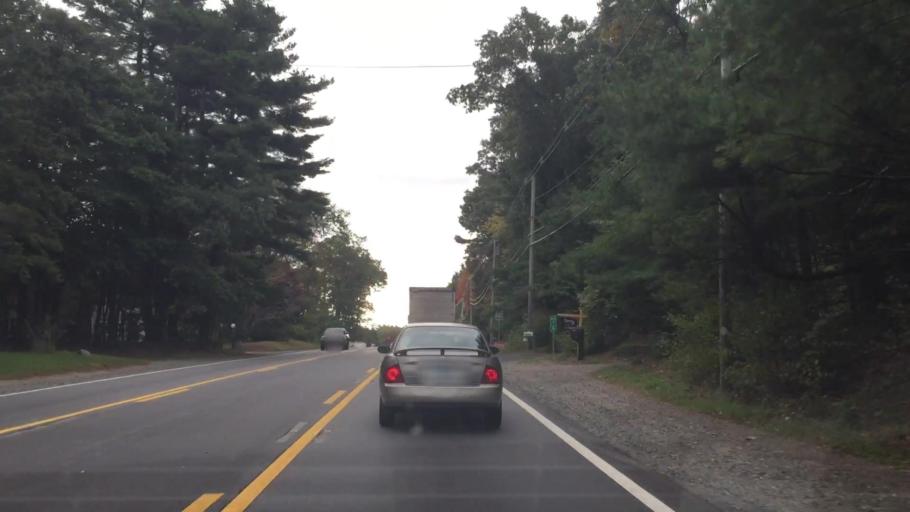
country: US
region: Massachusetts
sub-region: Middlesex County
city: North Reading
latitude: 42.6267
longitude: -71.0612
